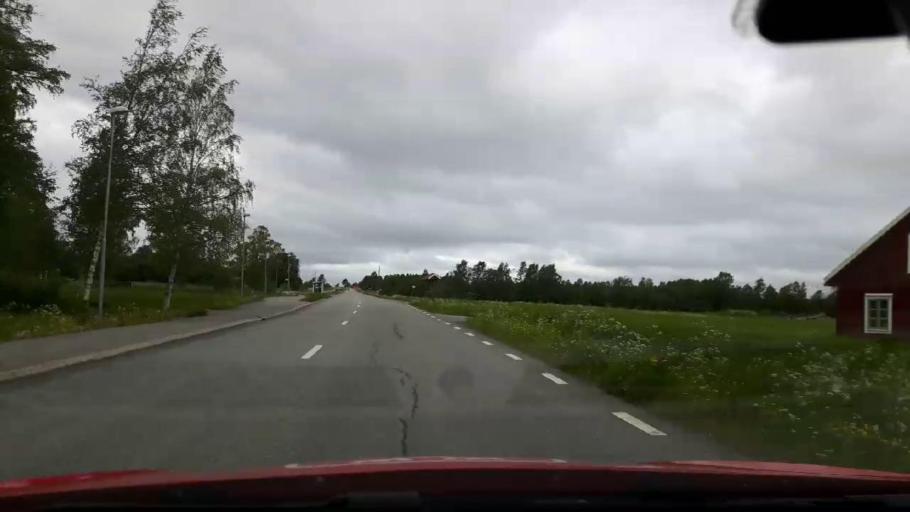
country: SE
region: Jaemtland
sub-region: OEstersunds Kommun
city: Ostersund
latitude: 63.2245
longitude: 14.5974
